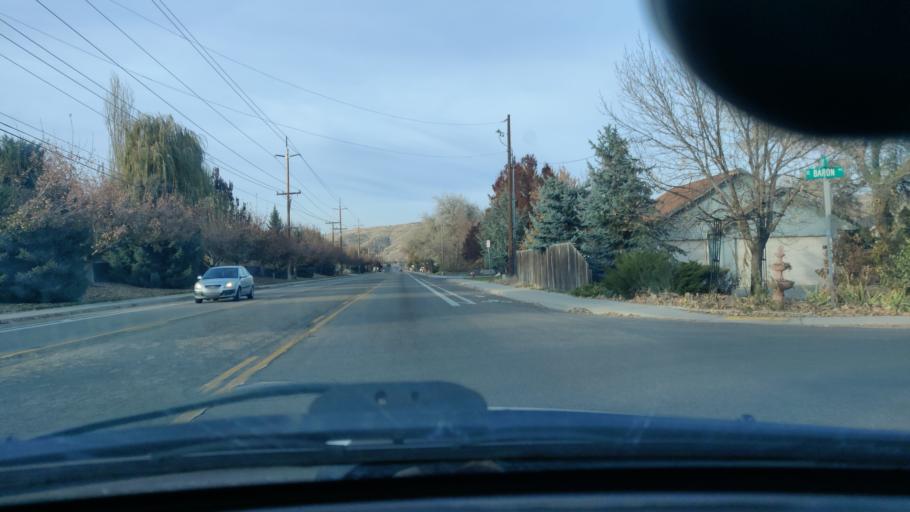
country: US
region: Idaho
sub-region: Ada County
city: Garden City
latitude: 43.6738
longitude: -116.2792
